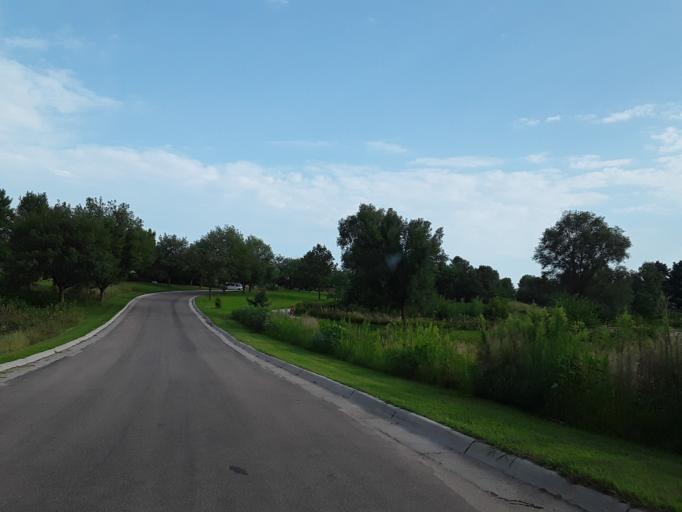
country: US
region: Nebraska
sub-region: Saunders County
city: Ashland
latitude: 41.0207
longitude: -96.3125
